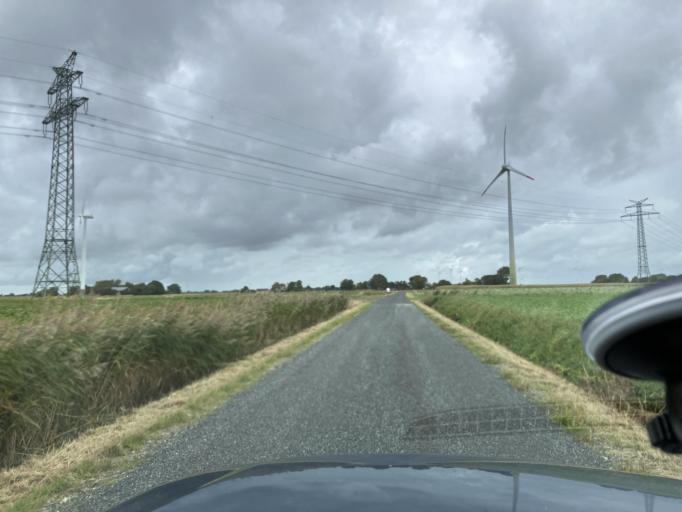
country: DE
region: Schleswig-Holstein
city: Wesselburen
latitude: 54.1950
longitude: 8.9552
